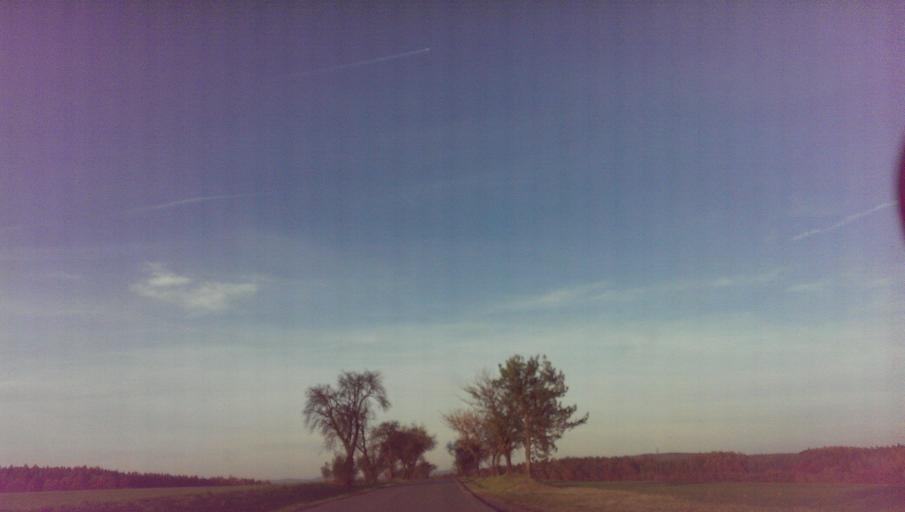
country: CZ
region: Zlin
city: Tecovice
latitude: 49.1765
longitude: 17.6051
